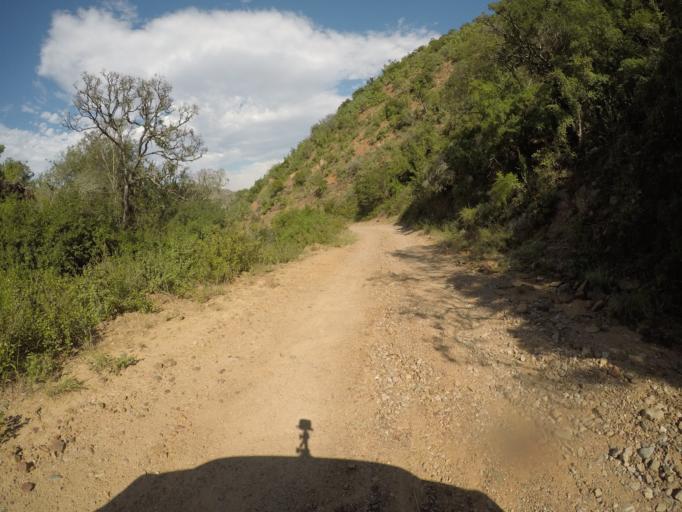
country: ZA
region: Eastern Cape
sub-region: Cacadu District Municipality
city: Kareedouw
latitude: -33.6565
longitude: 24.4012
